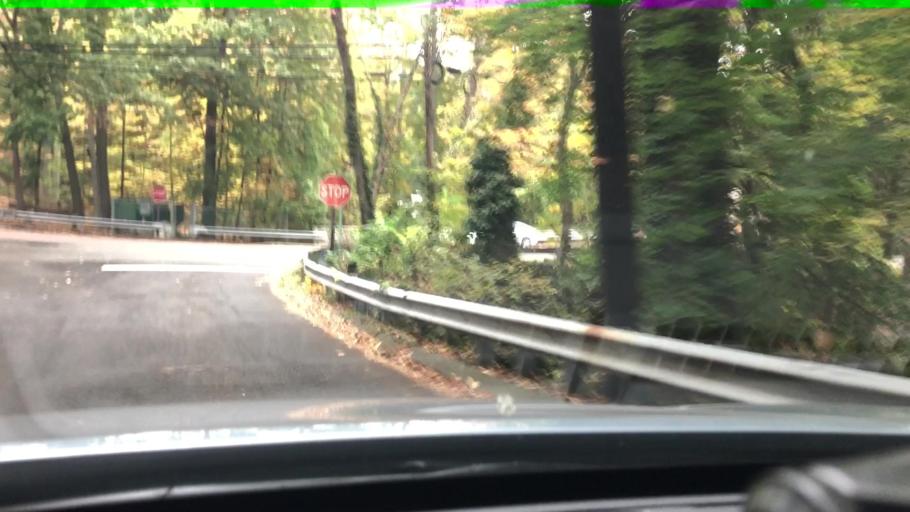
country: US
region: New Jersey
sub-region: Bergen County
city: Woodcliff Lake
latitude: 41.0346
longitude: -74.0643
